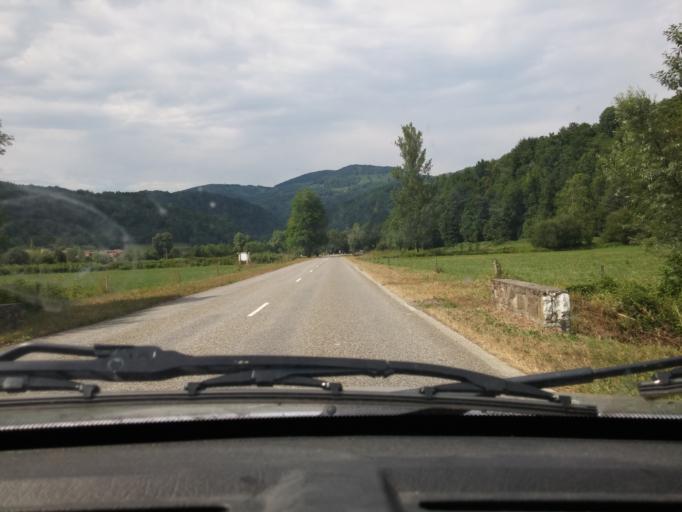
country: FR
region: Midi-Pyrenees
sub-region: Departement de l'Ariege
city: Saint-Girons
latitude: 42.8880
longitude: 1.2149
